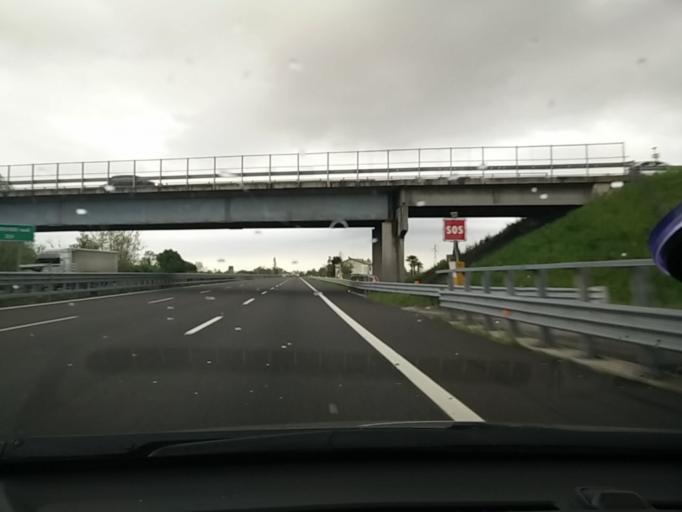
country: IT
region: Veneto
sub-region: Provincia di Treviso
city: San Floriano-Olmi
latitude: 45.6681
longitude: 12.3113
